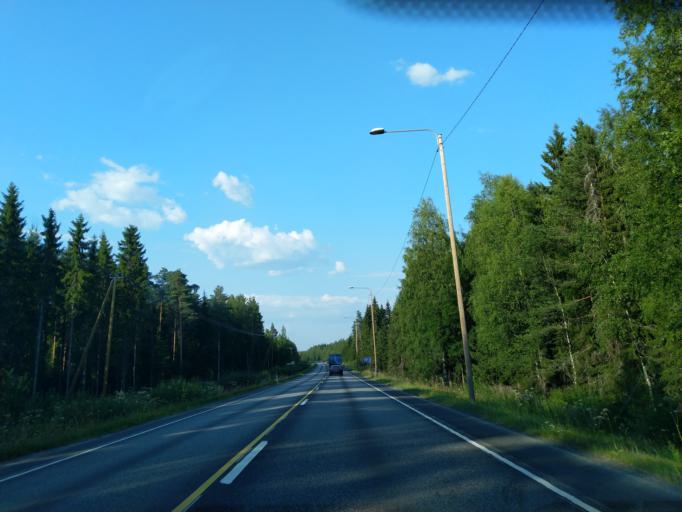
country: FI
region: Satakunta
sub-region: Pori
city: Pomarkku
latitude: 61.7079
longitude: 22.0290
